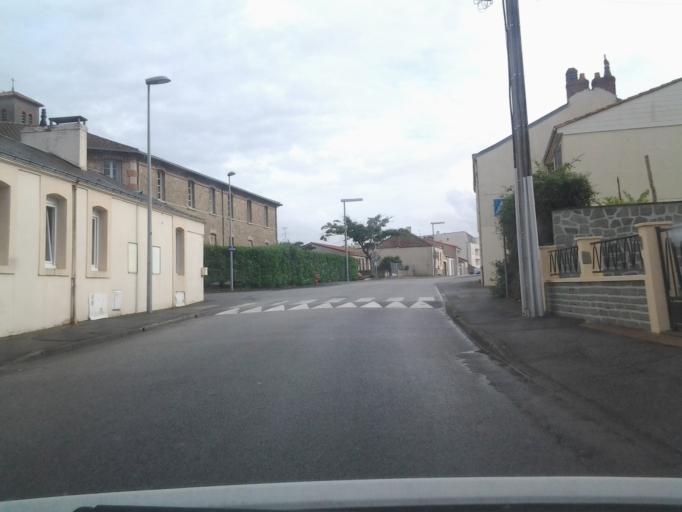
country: FR
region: Pays de la Loire
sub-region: Departement de la Vendee
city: La Roche-sur-Yon
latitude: 46.6767
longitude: -1.4213
